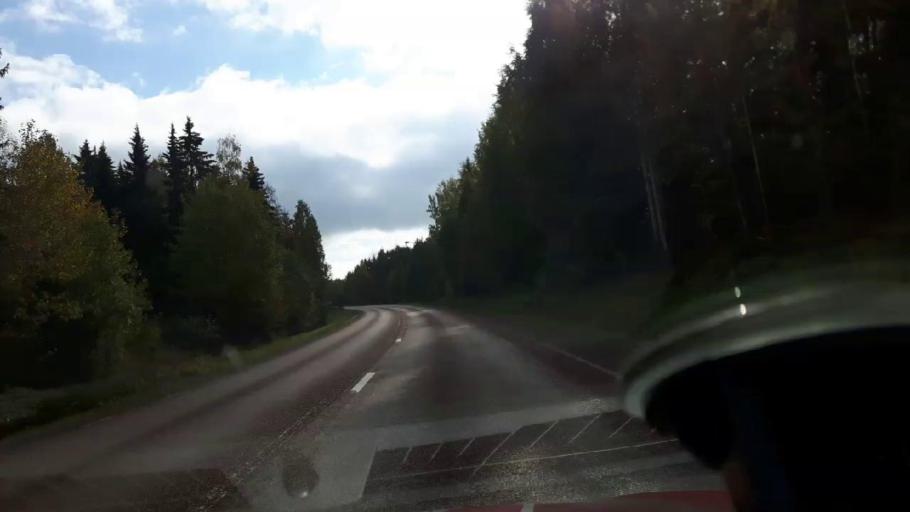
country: SE
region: Gaevleborg
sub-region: Bollnas Kommun
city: Arbra
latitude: 61.5754
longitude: 16.3179
